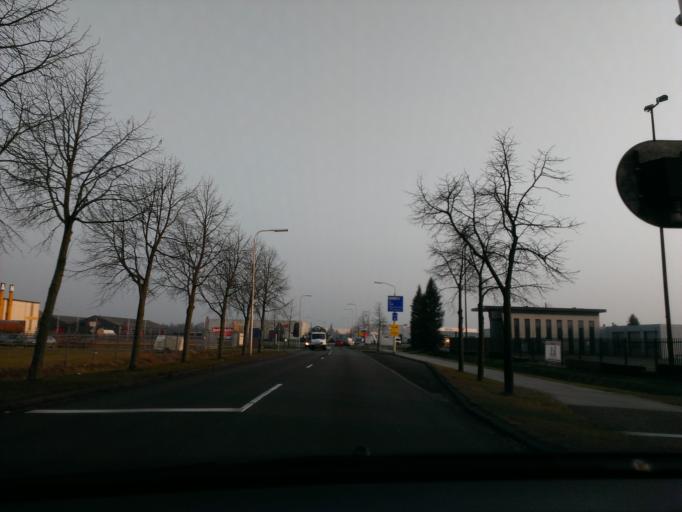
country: NL
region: Drenthe
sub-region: Gemeente Hoogeveen
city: Hoogeveen
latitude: 52.7275
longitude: 6.5210
